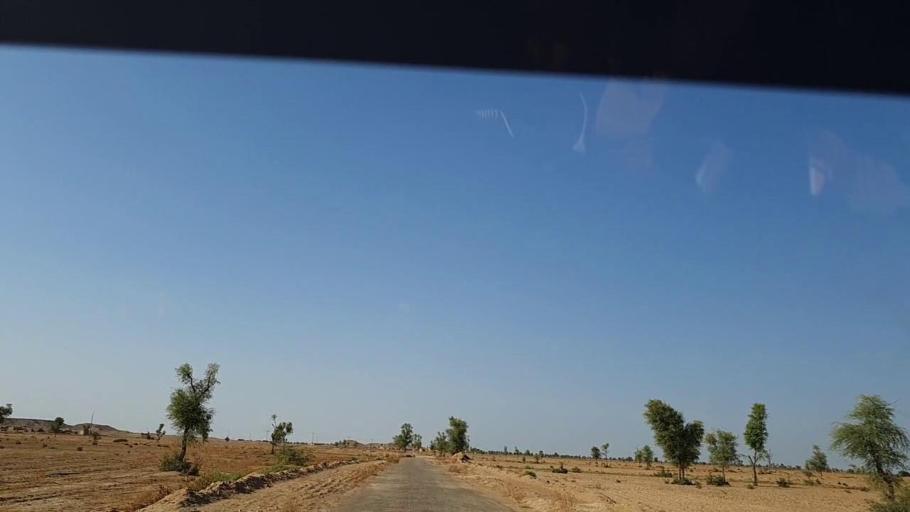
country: PK
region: Sindh
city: Johi
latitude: 26.5339
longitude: 67.5078
